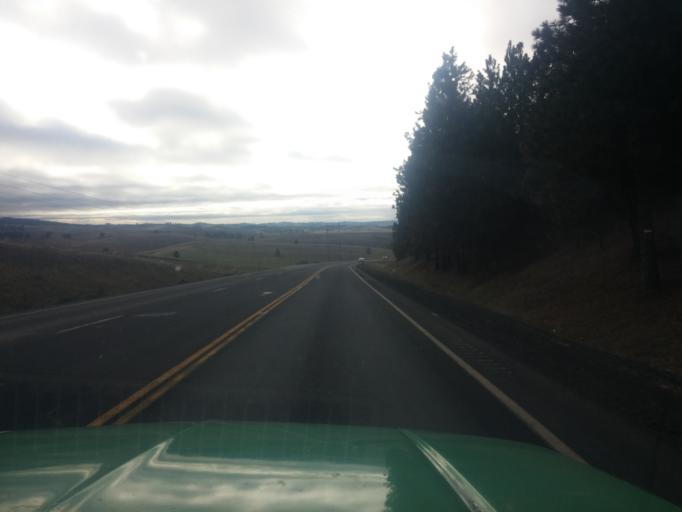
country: US
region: Idaho
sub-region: Latah County
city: Moscow
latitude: 46.8050
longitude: -117.0014
